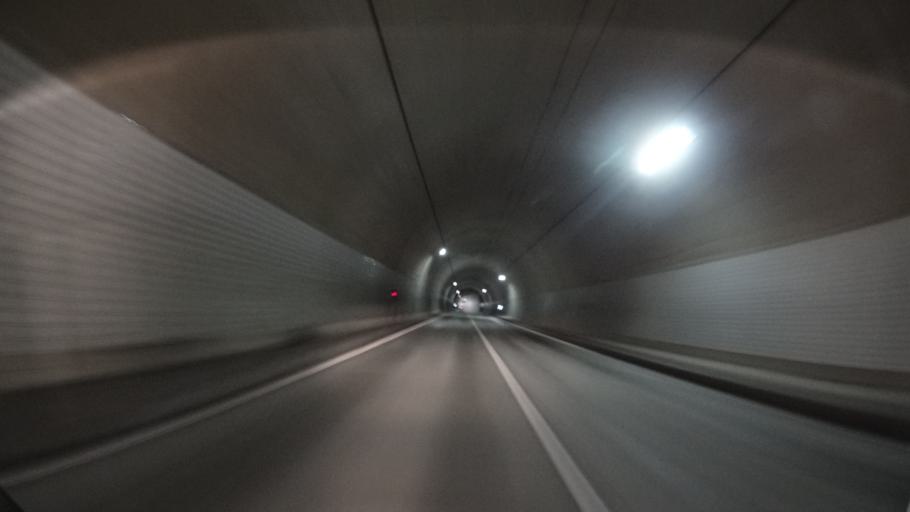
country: JP
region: Ehime
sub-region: Nishiuwa-gun
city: Ikata-cho
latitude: 33.4543
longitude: 132.2738
